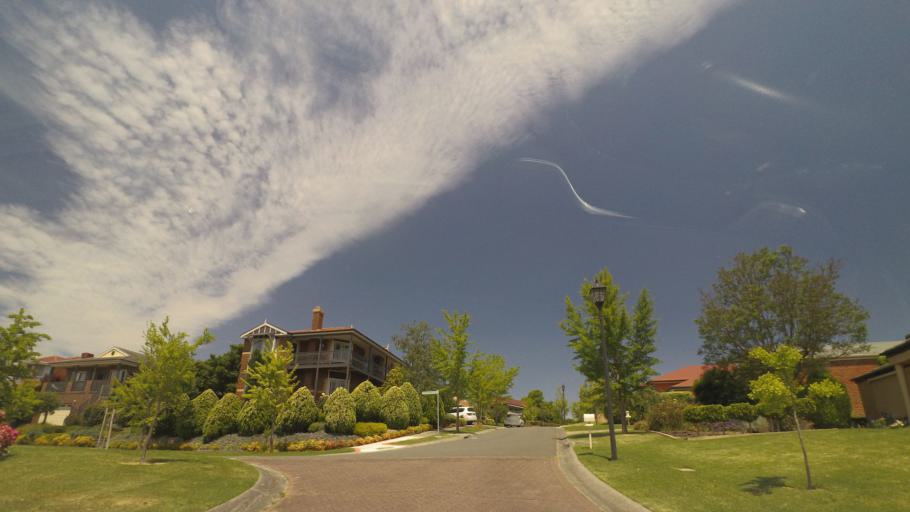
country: AU
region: Victoria
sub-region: Maroondah
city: Croydon North
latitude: -37.7599
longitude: 145.3030
